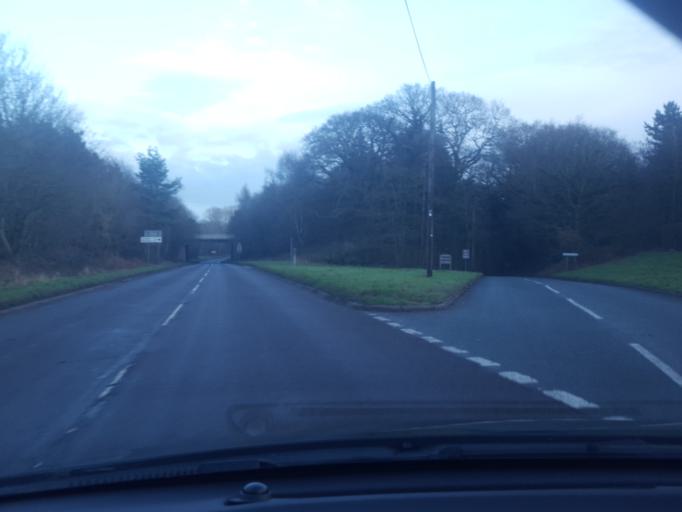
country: GB
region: England
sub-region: Shropshire
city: Tong
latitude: 52.6677
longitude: -2.3335
